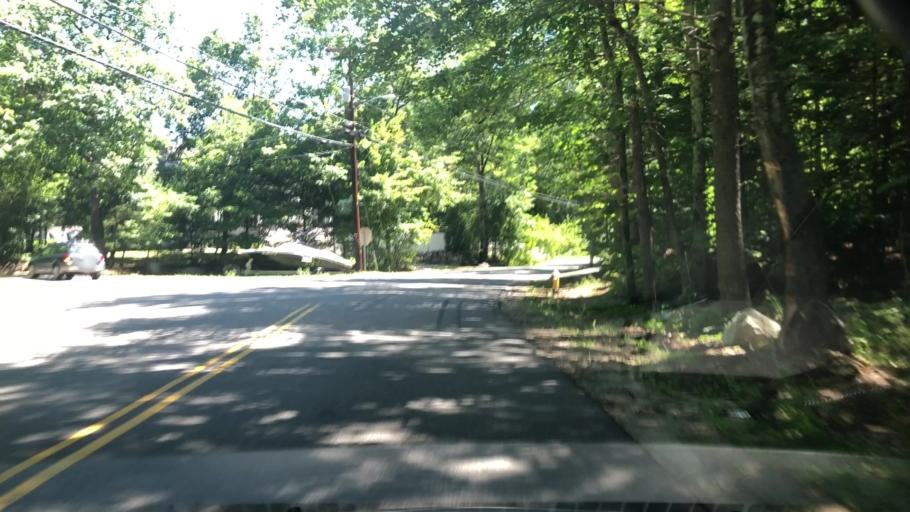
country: US
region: New Hampshire
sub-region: Hillsborough County
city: Milford
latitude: 42.8650
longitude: -71.6055
